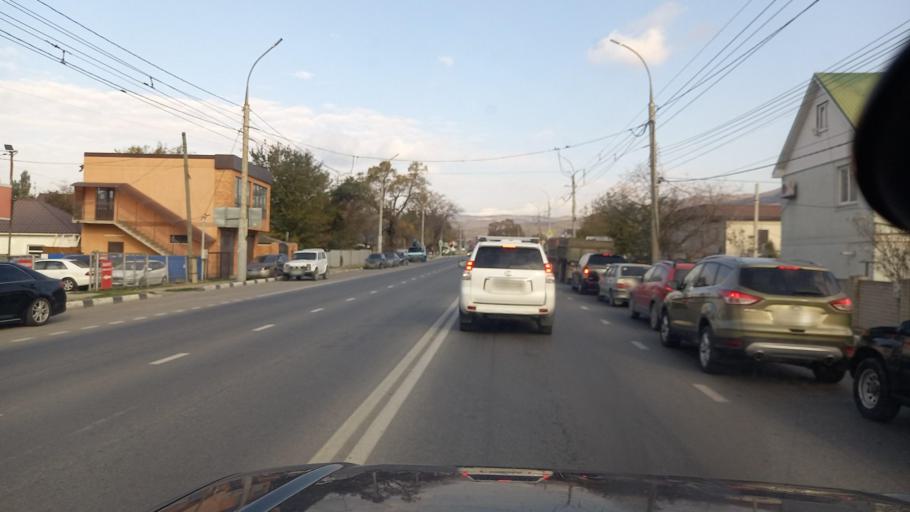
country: RU
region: Krasnodarskiy
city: Gayduk
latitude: 44.7536
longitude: 37.7267
